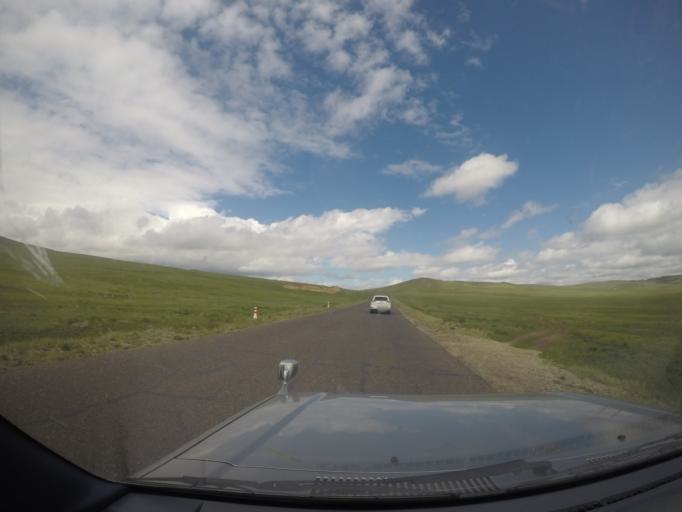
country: MN
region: Hentiy
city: Modot
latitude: 47.7956
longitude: 108.6892
